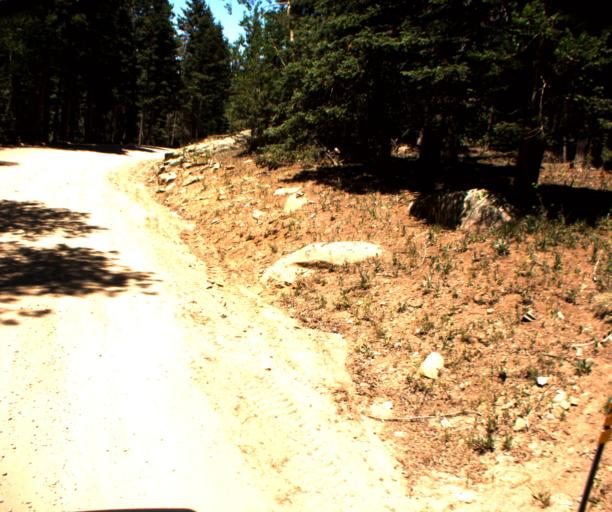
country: US
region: Arizona
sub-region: Graham County
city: Swift Trail Junction
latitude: 32.7001
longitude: -109.9102
